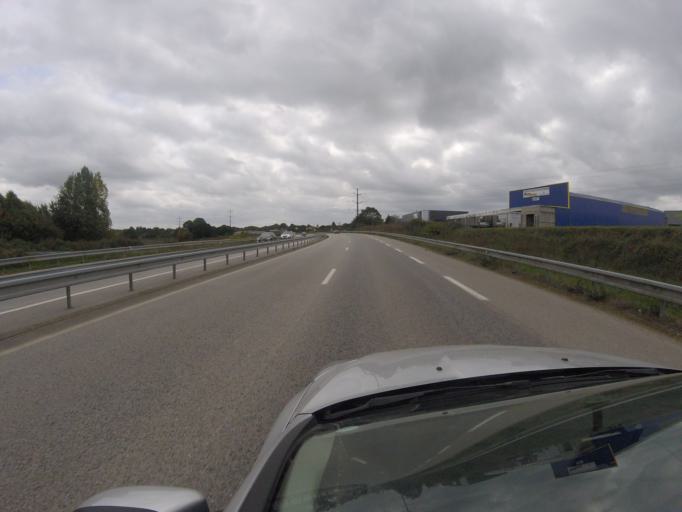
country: FR
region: Lower Normandy
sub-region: Departement de la Manche
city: La Glacerie
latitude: 49.5887
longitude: -1.5968
